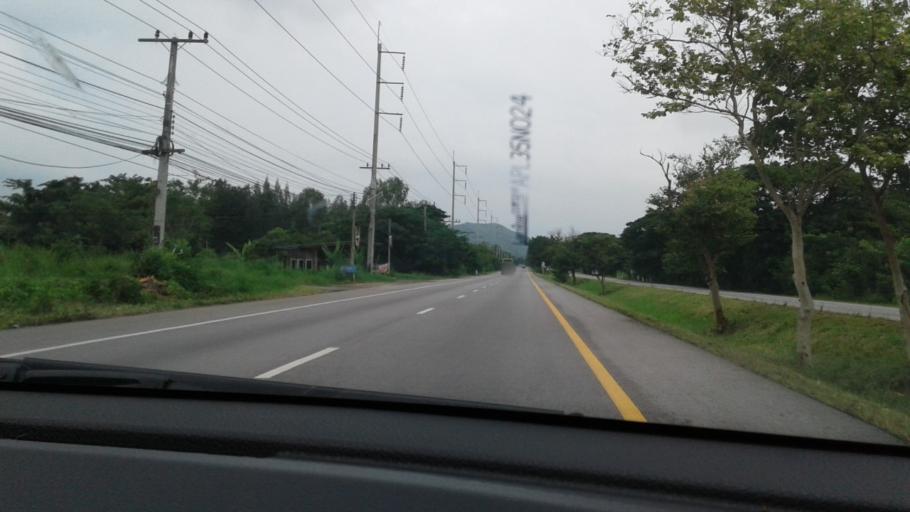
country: TH
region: Prachuap Khiri Khan
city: Prachuap Khiri Khan
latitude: 11.8800
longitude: 99.7880
